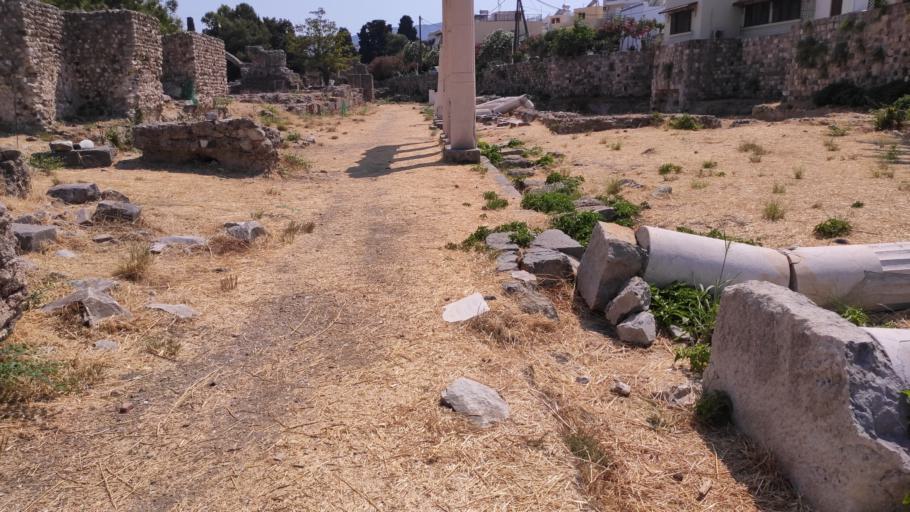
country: GR
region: South Aegean
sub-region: Nomos Dodekanisou
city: Kos
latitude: 36.8918
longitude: 27.2847
